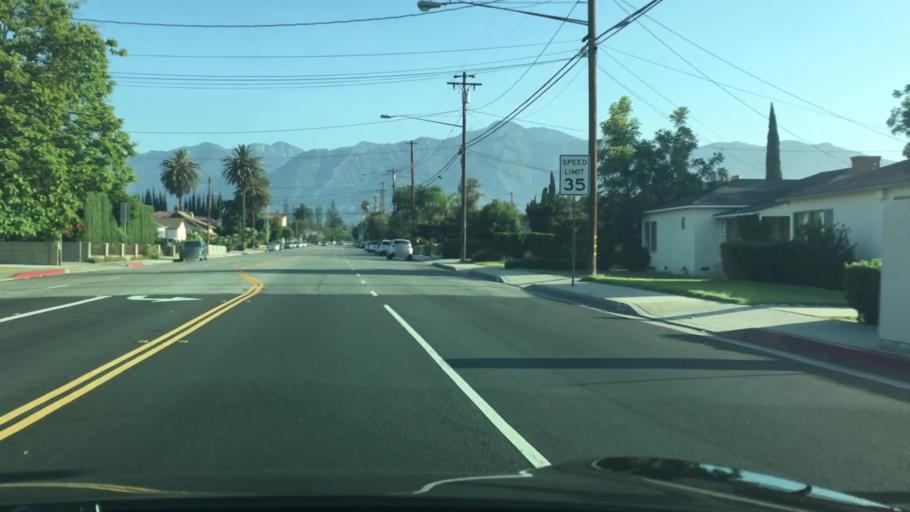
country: US
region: California
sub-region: Los Angeles County
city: Temple City
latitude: 34.1211
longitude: -118.0638
